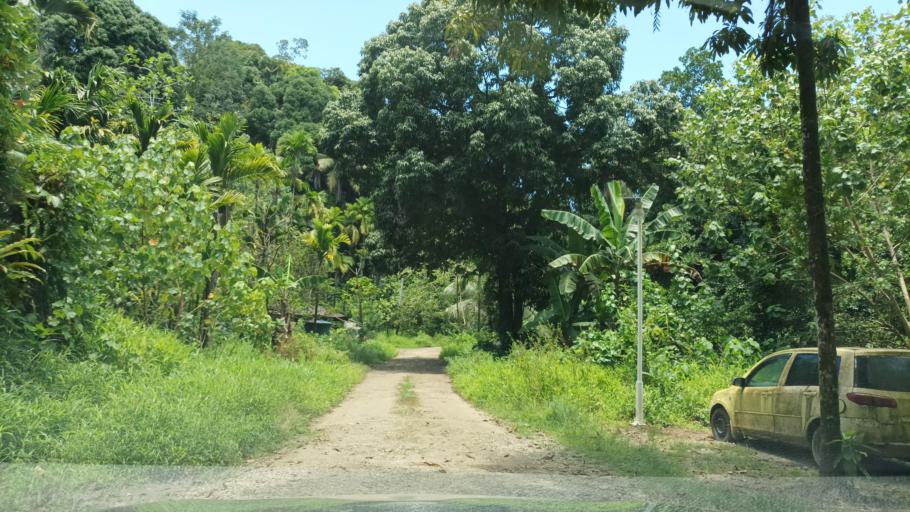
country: FM
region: Pohnpei
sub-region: Madolenihm Municipality
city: Madolenihm Municipality Government
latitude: 6.8442
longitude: 158.3181
